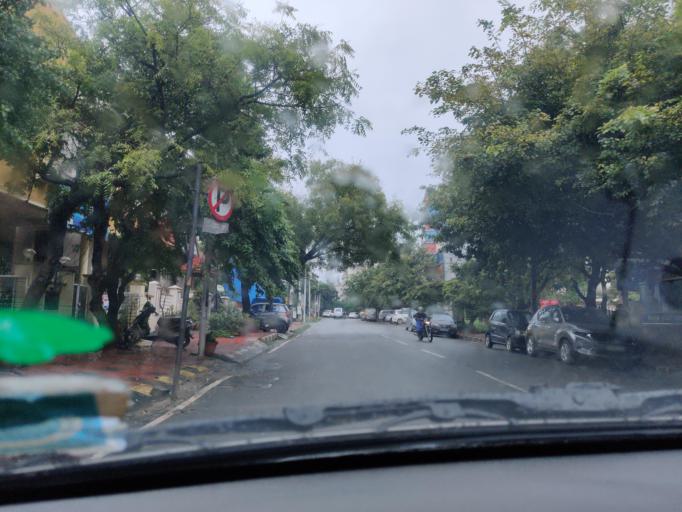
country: IN
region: Karnataka
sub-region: Bangalore Urban
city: Bangalore
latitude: 13.0244
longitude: 77.6398
